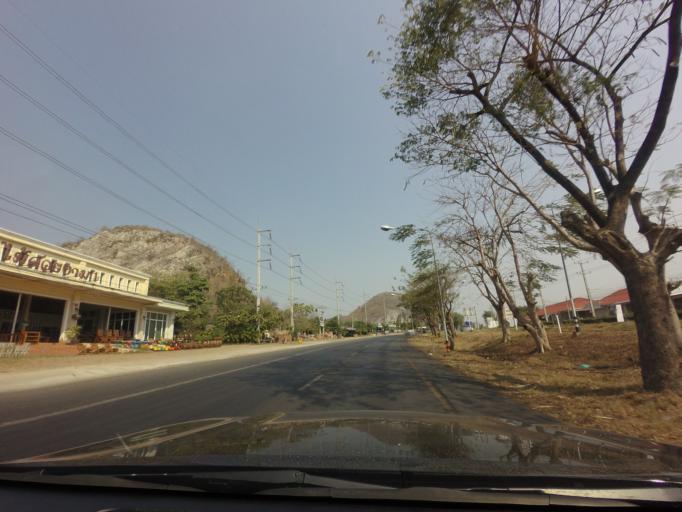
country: TH
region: Kanchanaburi
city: Kanchanaburi
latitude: 14.0652
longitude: 99.4982
